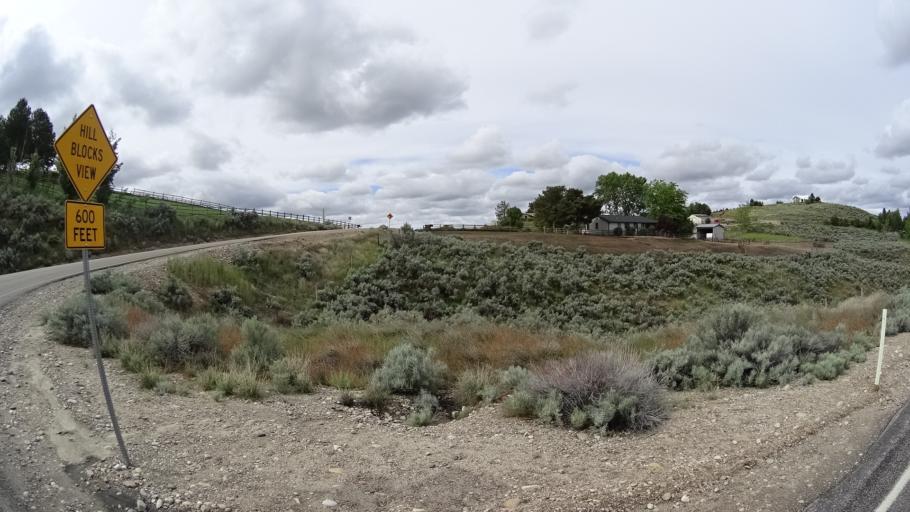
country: US
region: Idaho
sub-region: Ada County
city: Eagle
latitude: 43.7416
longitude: -116.3555
